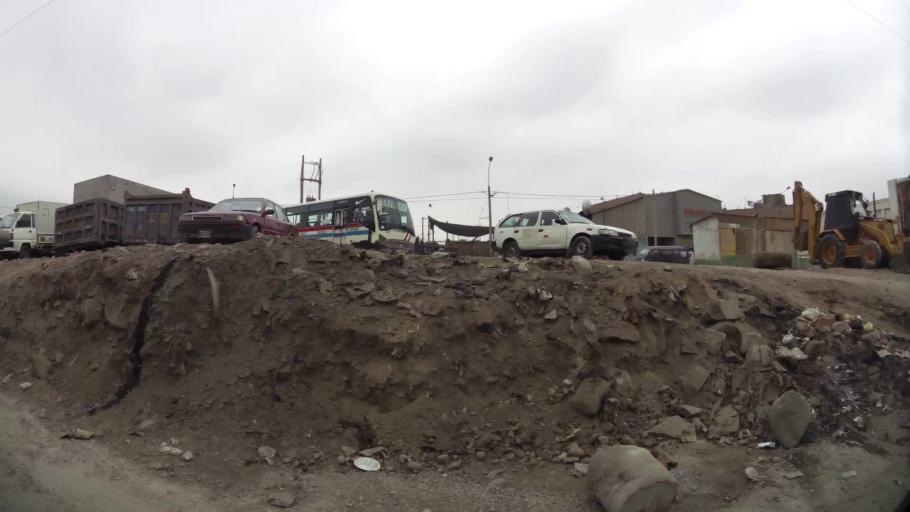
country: PE
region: Lima
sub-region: Lima
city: Independencia
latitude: -11.9726
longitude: -77.0891
